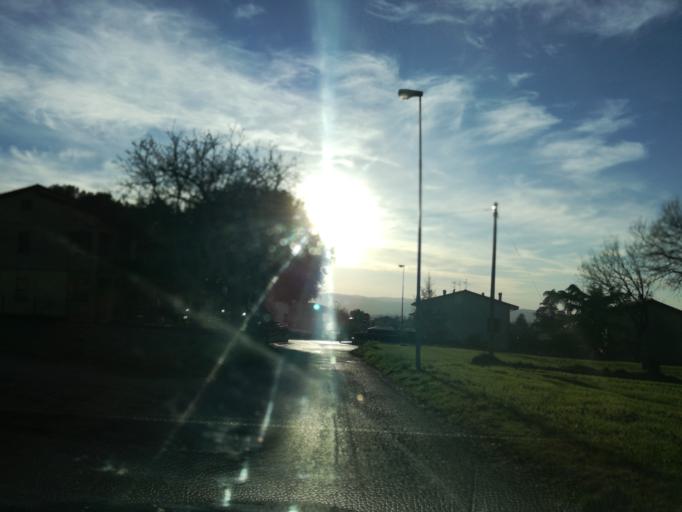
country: IT
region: Umbria
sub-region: Provincia di Perugia
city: Rivotorto
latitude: 43.0466
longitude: 12.6210
